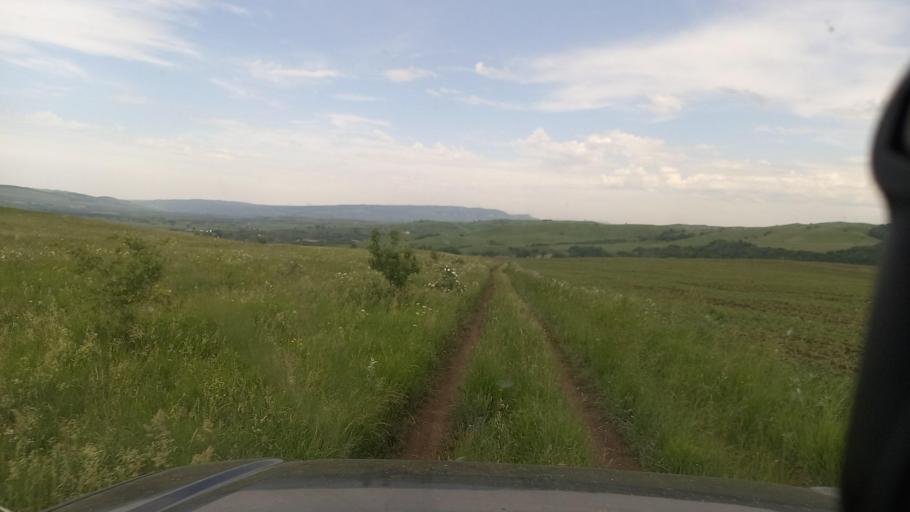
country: RU
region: Krasnodarskiy
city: Peredovaya
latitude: 44.0787
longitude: 41.3381
